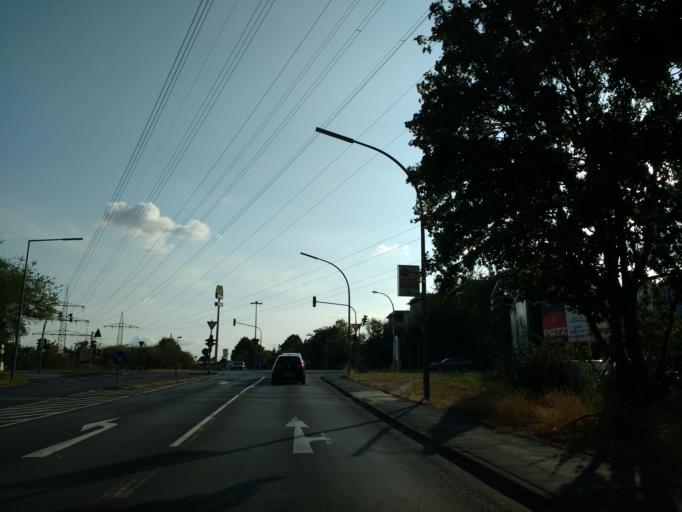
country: DE
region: North Rhine-Westphalia
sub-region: Regierungsbezirk Koln
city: Gremberghoven
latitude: 50.9128
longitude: 7.0562
